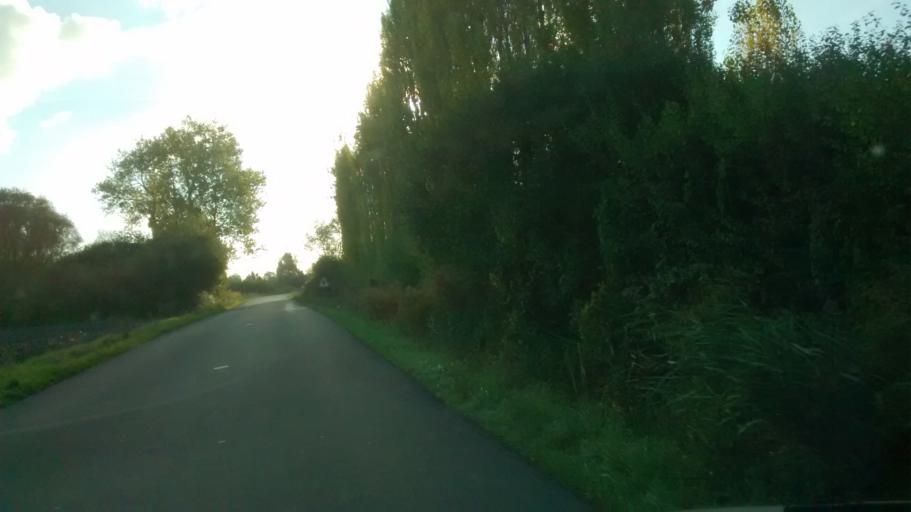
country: FR
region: Brittany
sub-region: Departement d'Ille-et-Vilaine
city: Saint-Meloir-des-Ondes
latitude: 48.6293
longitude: -1.8770
